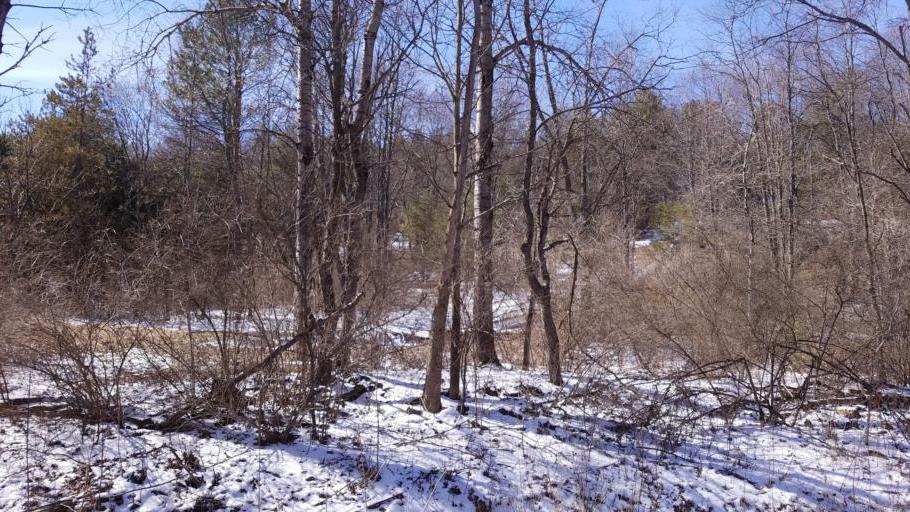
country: US
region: Pennsylvania
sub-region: Potter County
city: Galeton
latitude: 41.9135
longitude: -77.7489
